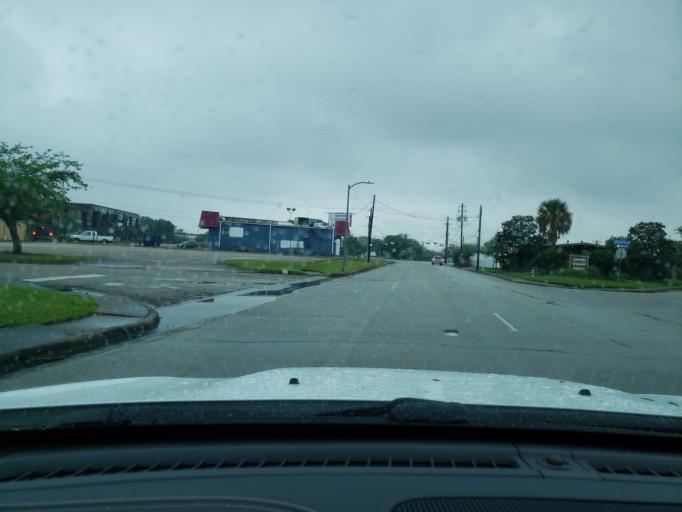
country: US
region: Texas
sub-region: Harris County
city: Baytown
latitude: 29.7366
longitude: -94.9766
